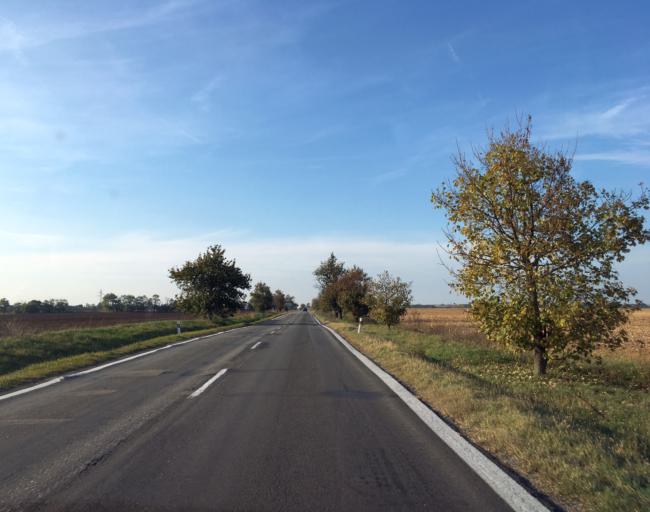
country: SK
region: Nitriansky
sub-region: Okres Nove Zamky
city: Nove Zamky
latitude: 48.0315
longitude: 18.1317
